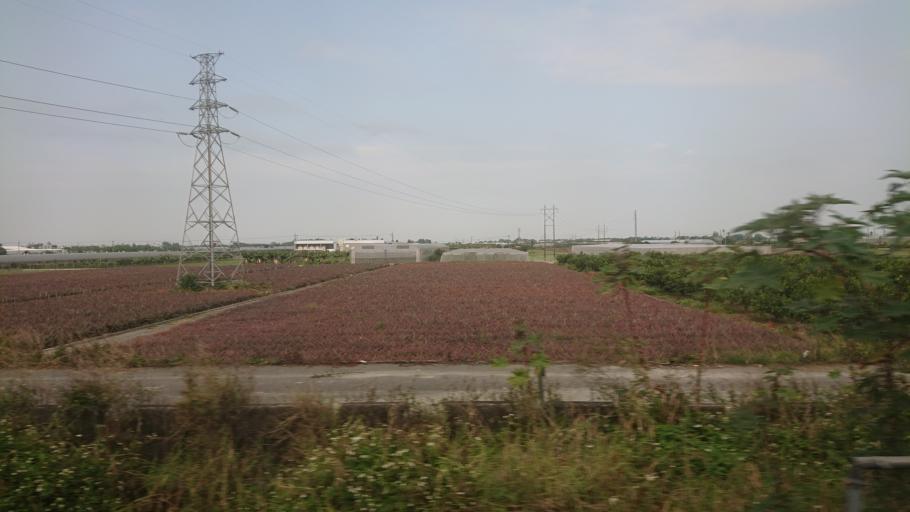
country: TW
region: Taiwan
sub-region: Yunlin
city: Douliu
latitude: 23.7352
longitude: 120.5833
